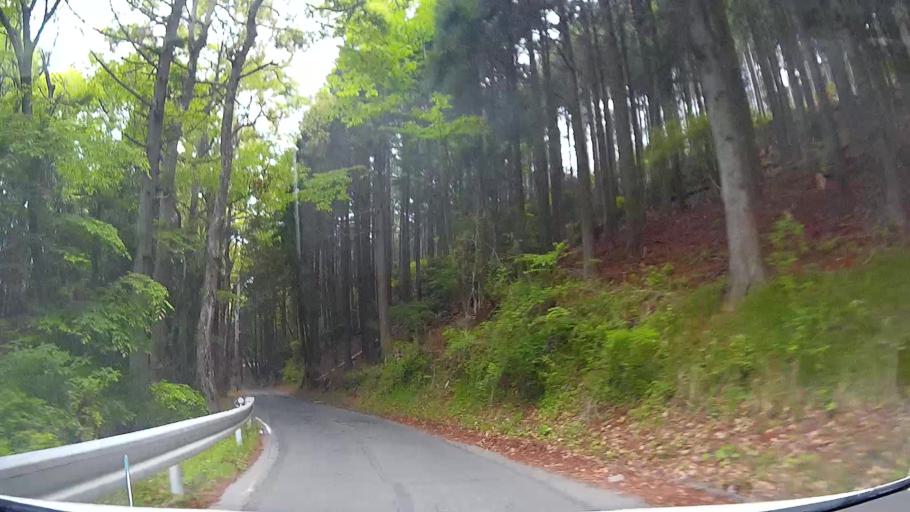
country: JP
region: Shizuoka
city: Ito
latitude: 34.9126
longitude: 139.0508
